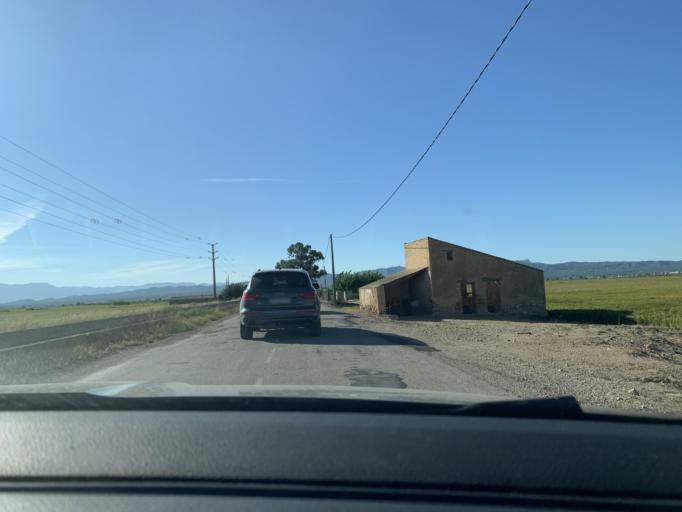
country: ES
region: Catalonia
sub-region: Provincia de Tarragona
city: Deltebre
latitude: 40.7511
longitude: 0.7230
